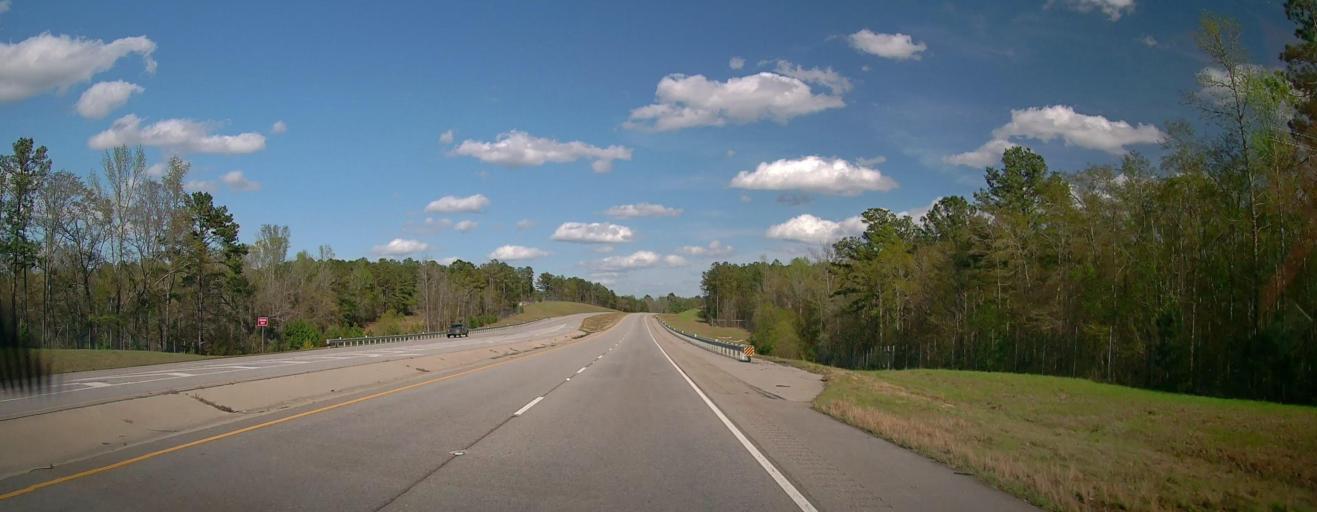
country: US
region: Georgia
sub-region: Baldwin County
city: Hardwick
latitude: 33.0404
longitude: -83.1321
